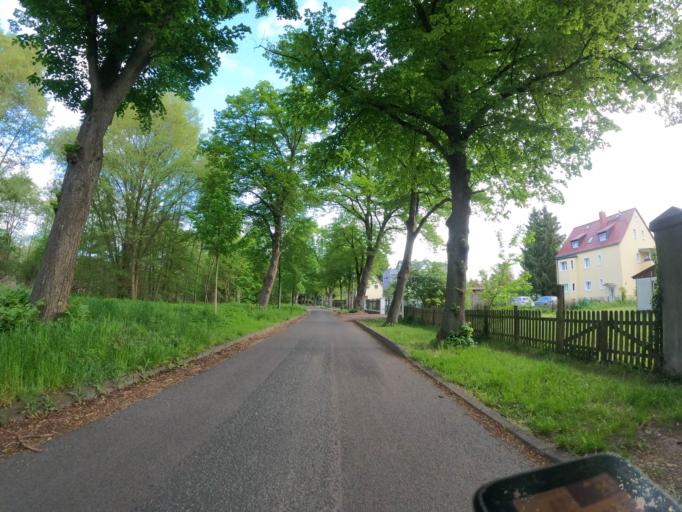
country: DE
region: Brandenburg
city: Konigs Wusterhausen
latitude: 52.2975
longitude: 13.6469
